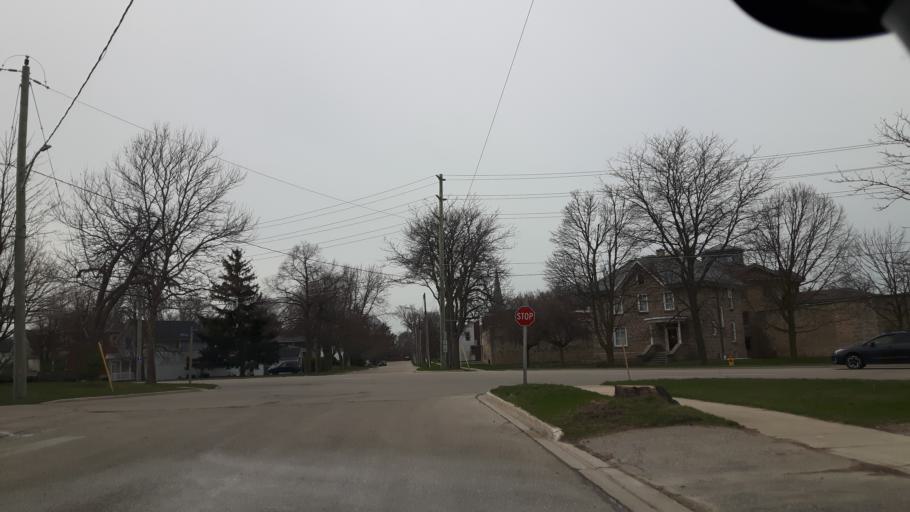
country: CA
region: Ontario
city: Goderich
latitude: 43.7498
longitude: -81.7074
